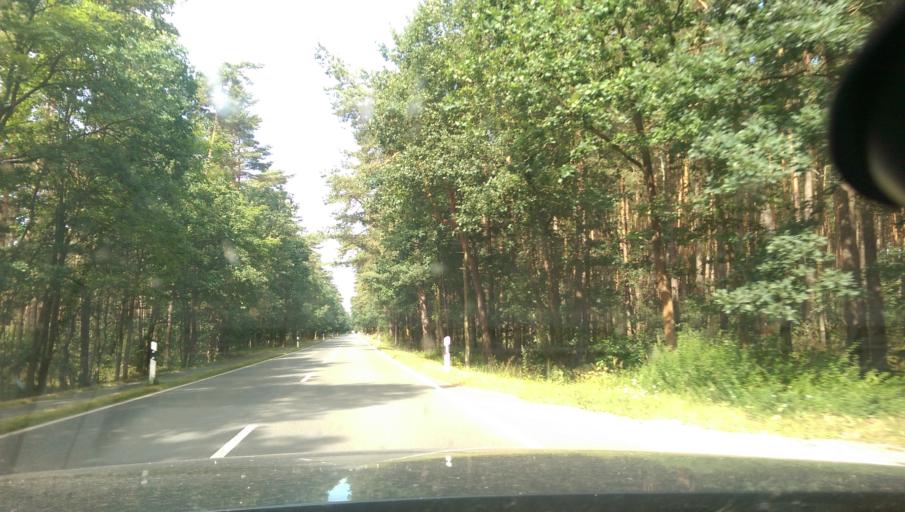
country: DE
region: Lower Saxony
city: Wietze
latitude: 52.6744
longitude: 9.8569
